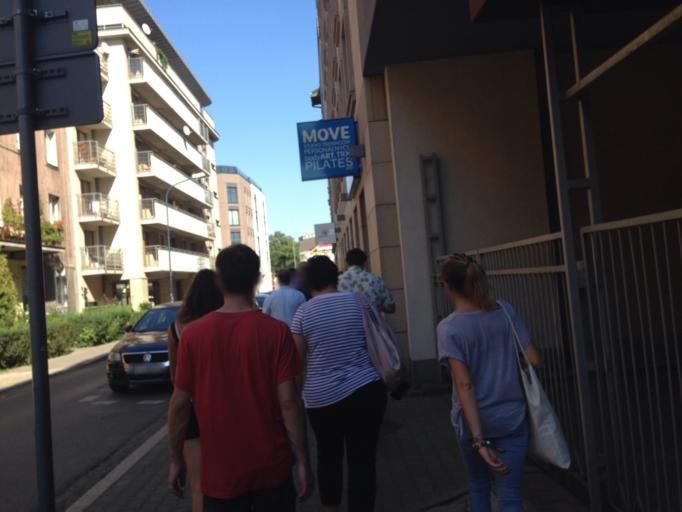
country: PL
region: Lesser Poland Voivodeship
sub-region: Krakow
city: Krakow
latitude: 50.0470
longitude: 19.9529
